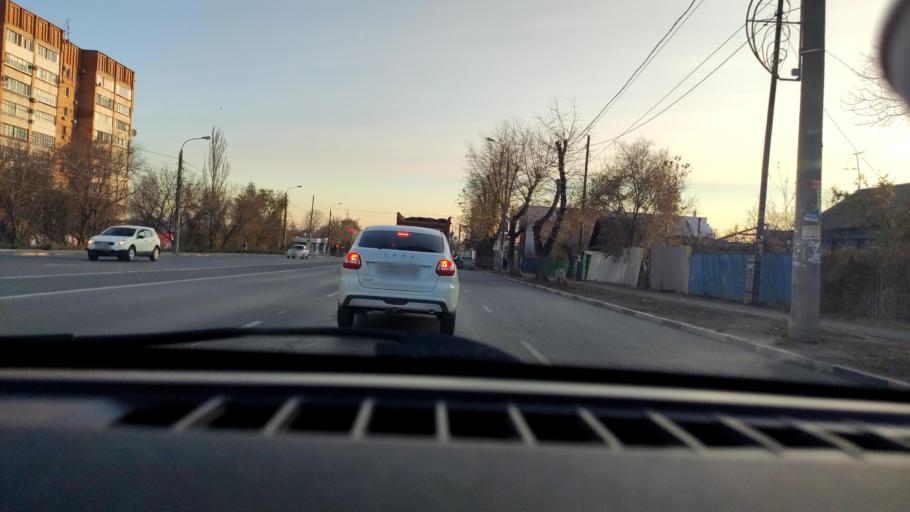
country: RU
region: Samara
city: Samara
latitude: 53.1863
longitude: 50.1912
